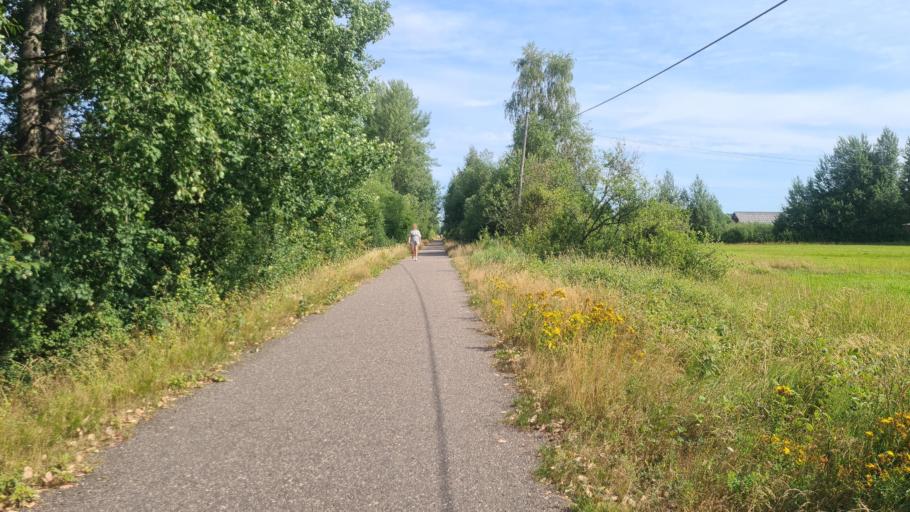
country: SE
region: Kronoberg
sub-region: Ljungby Kommun
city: Ljungby
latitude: 56.8484
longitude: 13.9665
